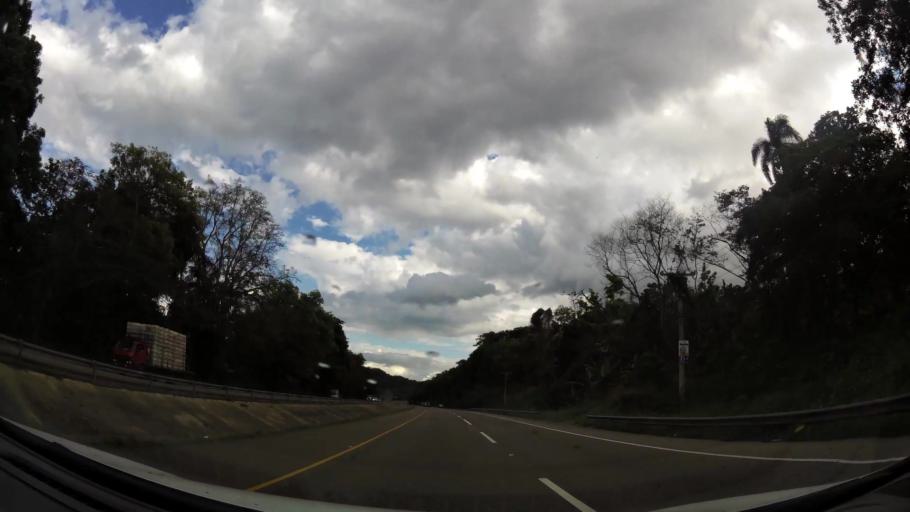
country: DO
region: La Vega
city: Rincon
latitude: 19.1393
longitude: -70.4663
